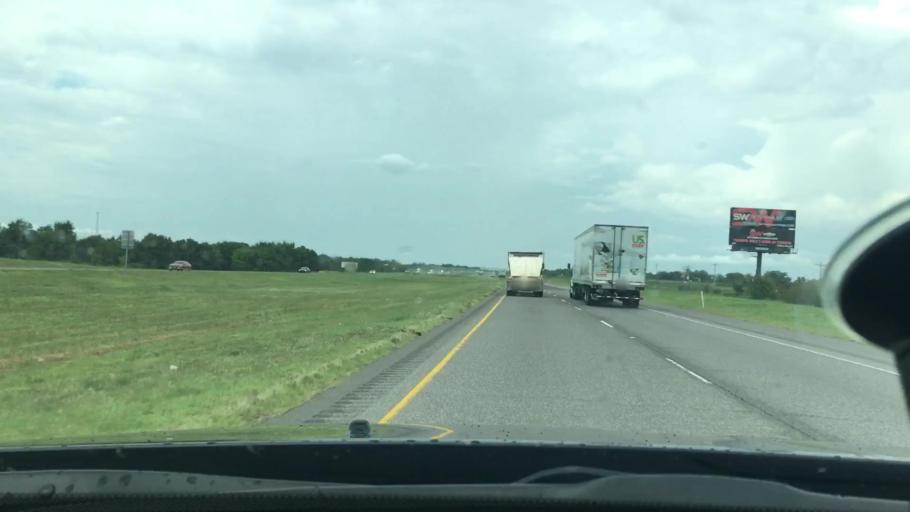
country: US
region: Oklahoma
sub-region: Garvin County
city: Wynnewood
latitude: 34.5601
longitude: -97.1933
